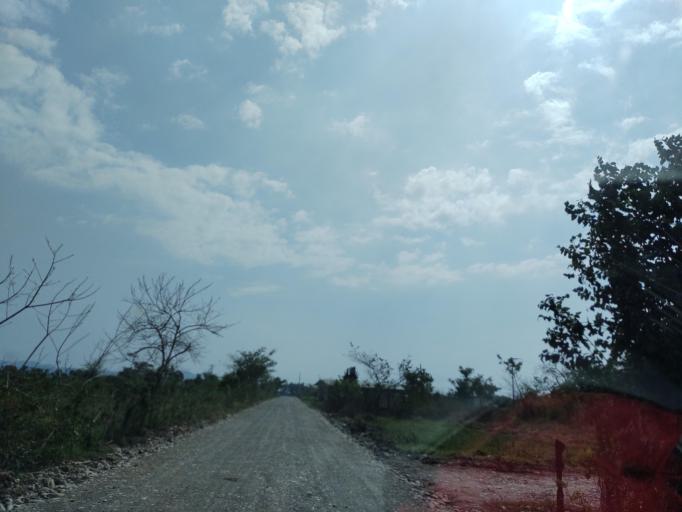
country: MX
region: Puebla
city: Espinal
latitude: 20.2814
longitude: -97.3337
